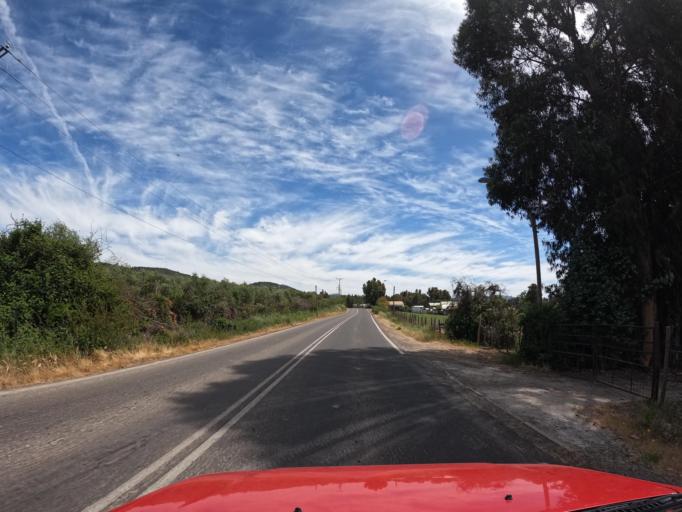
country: CL
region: Maule
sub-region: Provincia de Talca
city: Talca
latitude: -35.1149
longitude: -71.6383
